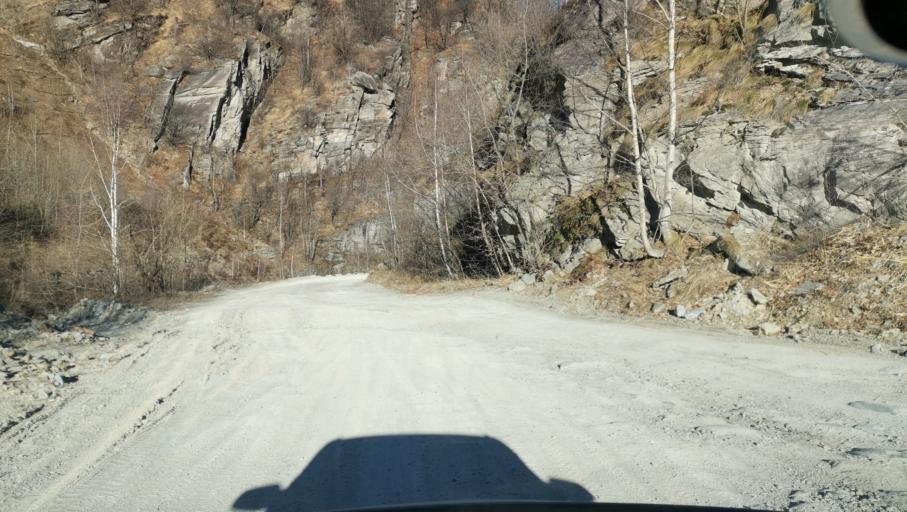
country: IT
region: Piedmont
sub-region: Provincia di Torino
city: Rora
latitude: 44.7657
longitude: 7.2004
